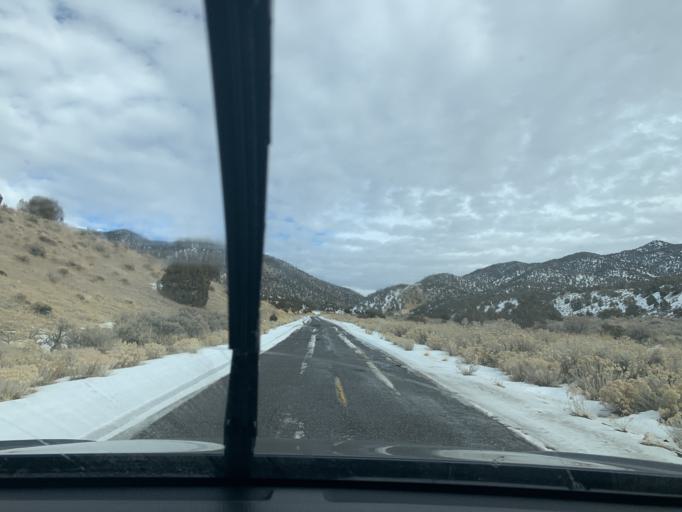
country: US
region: Utah
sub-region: Tooele County
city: Tooele
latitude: 40.3048
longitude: -112.2622
